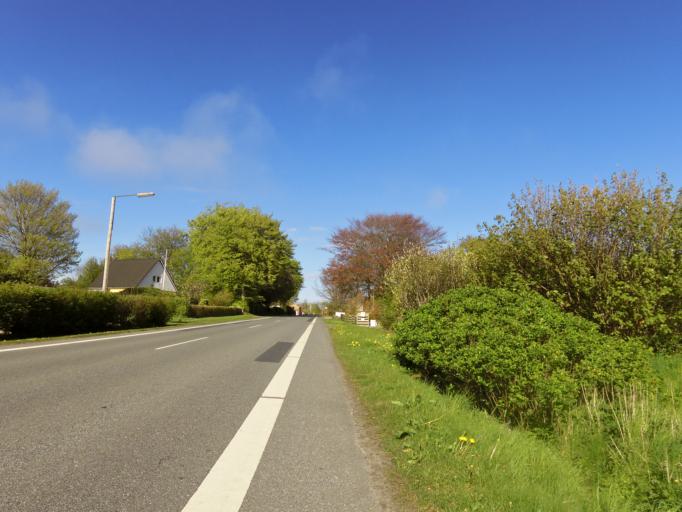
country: DK
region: South Denmark
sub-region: Tonder Kommune
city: Sherrebek
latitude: 55.1559
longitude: 8.8108
